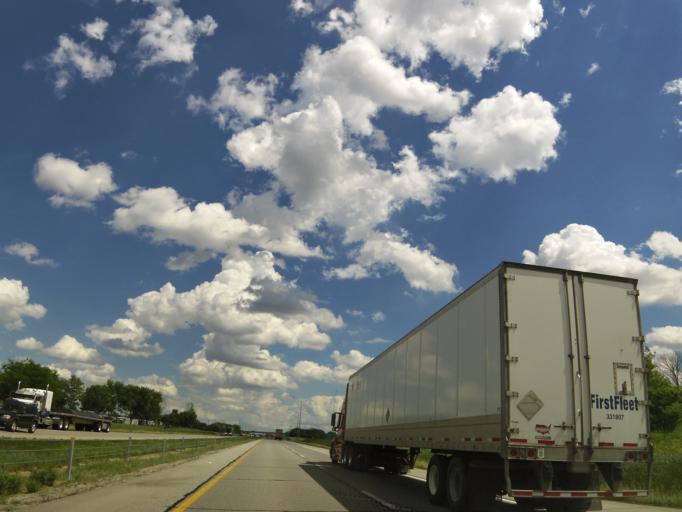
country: US
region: Iowa
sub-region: Linn County
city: Hiawatha
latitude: 42.0497
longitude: -91.6925
